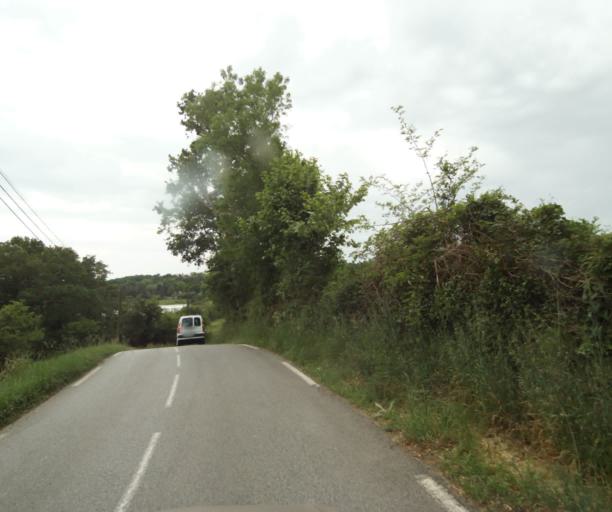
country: FR
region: Aquitaine
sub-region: Departement des Pyrenees-Atlantiques
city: Mouguerre
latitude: 43.4583
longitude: -1.4123
